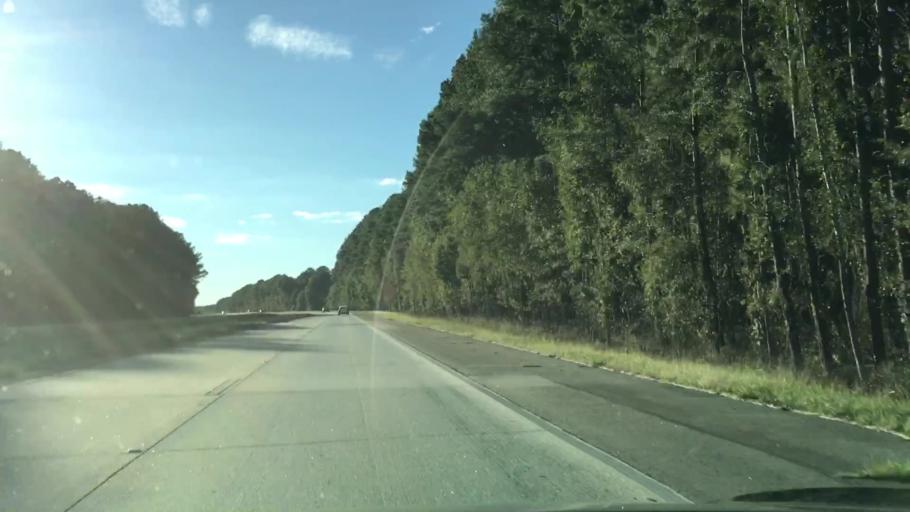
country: US
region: Georgia
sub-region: Greene County
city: Greensboro
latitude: 33.5494
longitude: -83.1293
